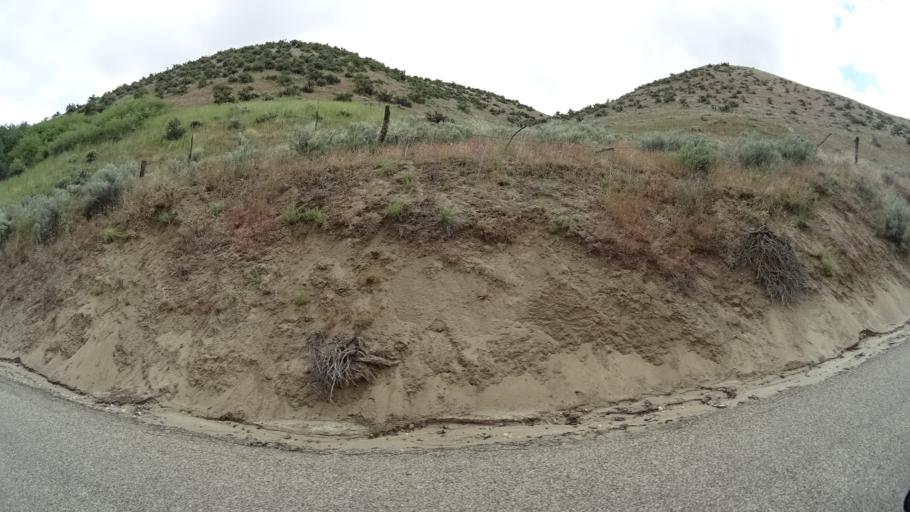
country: US
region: Idaho
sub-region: Ada County
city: Garden City
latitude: 43.6921
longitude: -116.2407
